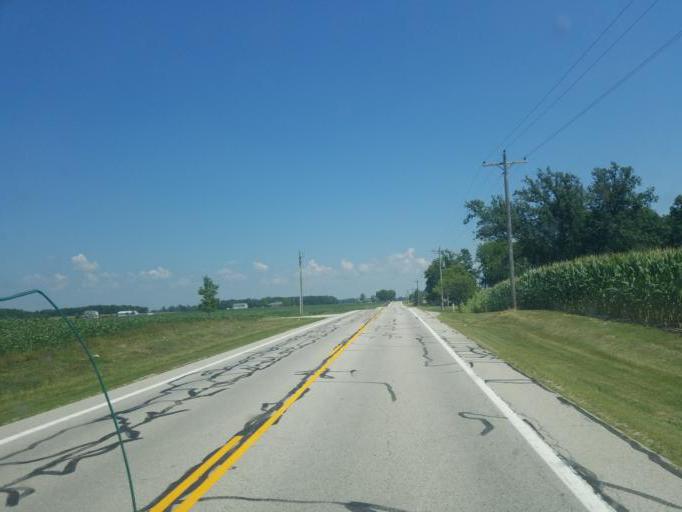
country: US
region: Ohio
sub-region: Shelby County
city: Anna
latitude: 40.3952
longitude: -84.1409
